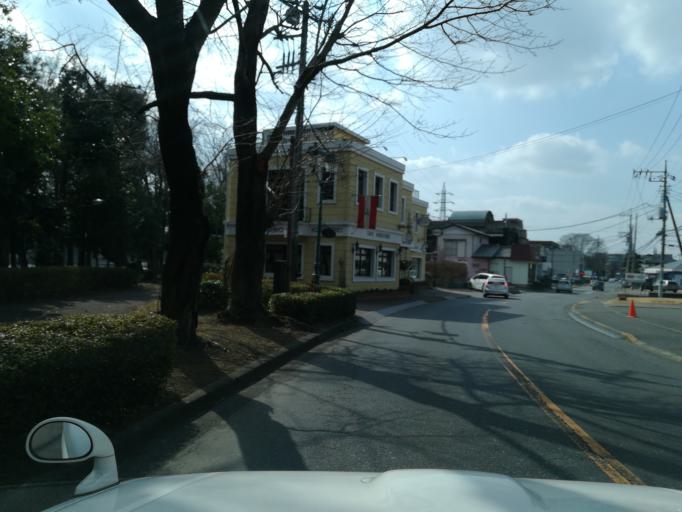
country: JP
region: Ibaraki
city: Naka
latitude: 36.0630
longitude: 140.1249
